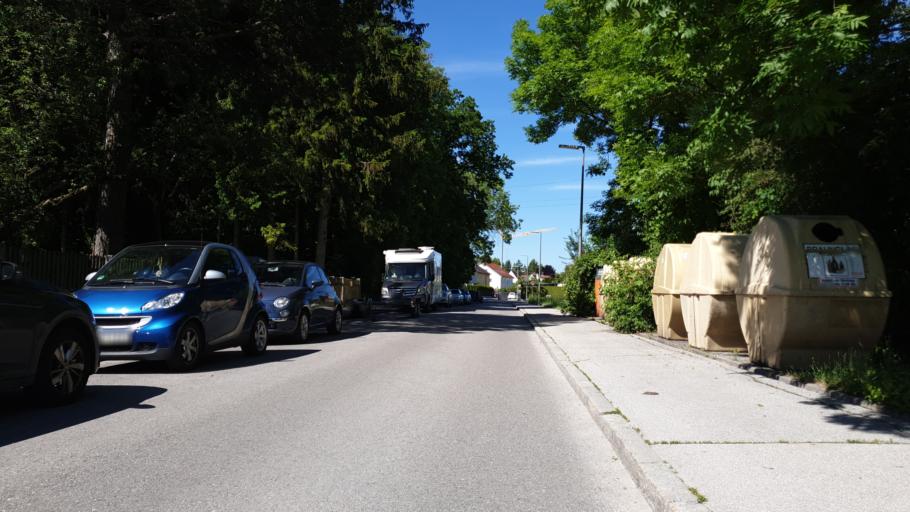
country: DE
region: Bavaria
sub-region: Upper Bavaria
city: Karlsfeld
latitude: 48.2005
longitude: 11.4490
